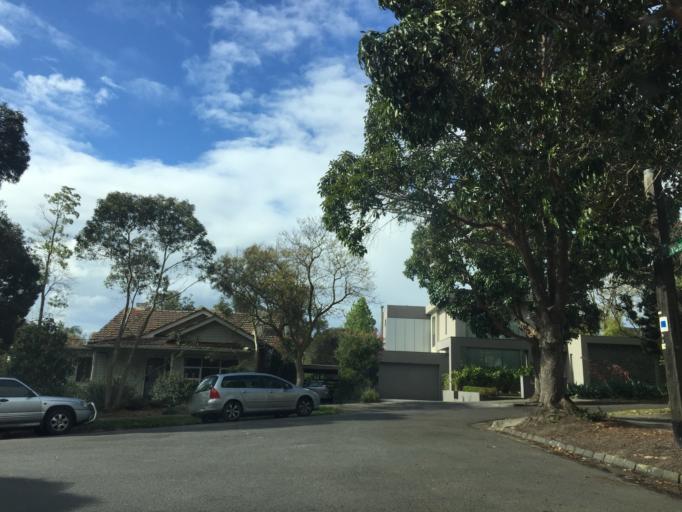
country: AU
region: Victoria
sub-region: Boroondara
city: Kew East
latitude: -37.8051
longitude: 145.0562
